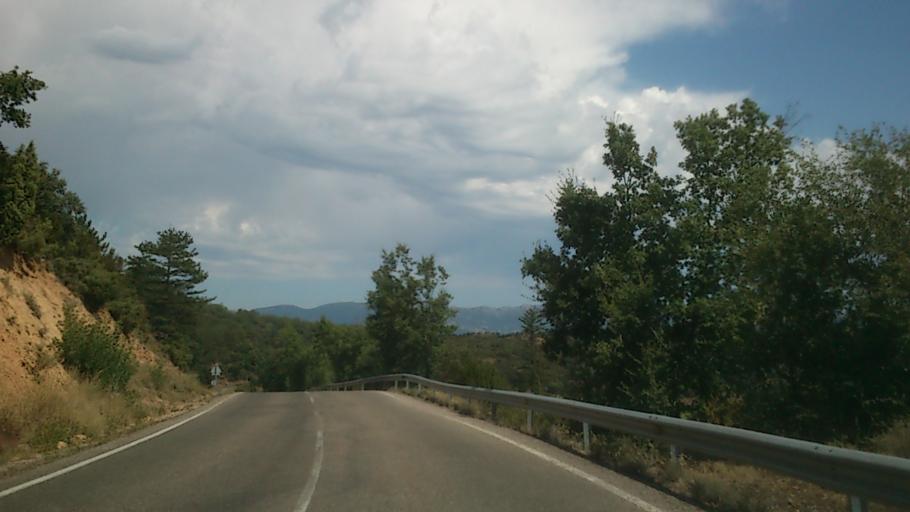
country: ES
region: Castille and Leon
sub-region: Provincia de Burgos
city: Frias
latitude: 42.7511
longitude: -3.3054
